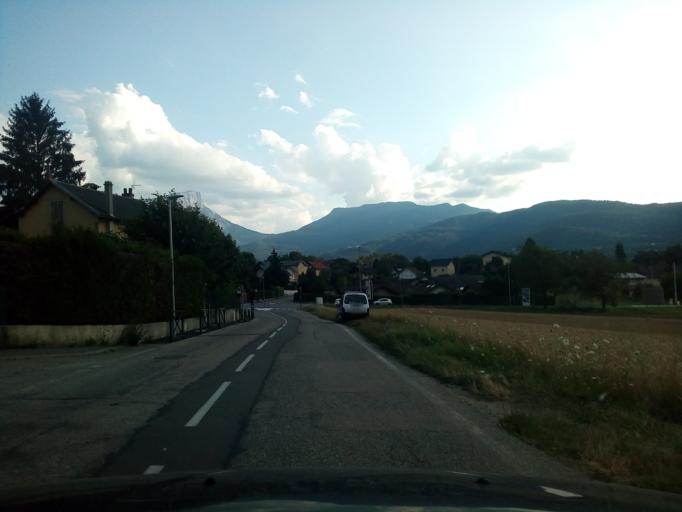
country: FR
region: Rhone-Alpes
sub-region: Departement de la Savoie
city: Challes-les-Eaux
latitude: 45.5449
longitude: 5.9795
